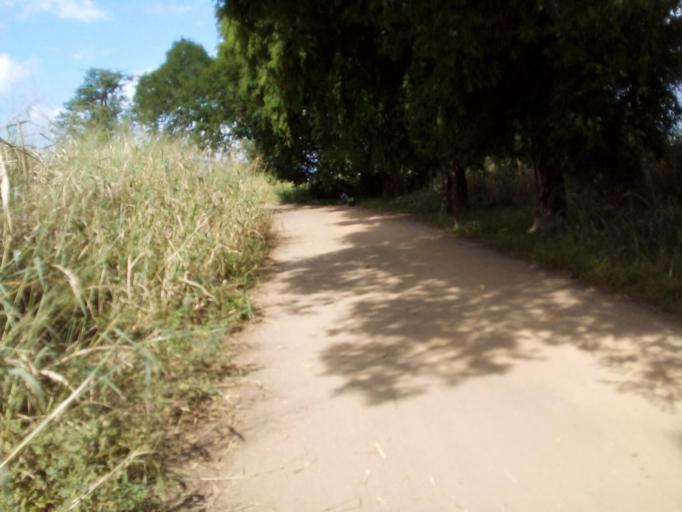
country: MZ
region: Zambezia
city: Quelimane
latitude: -17.5514
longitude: 36.6953
